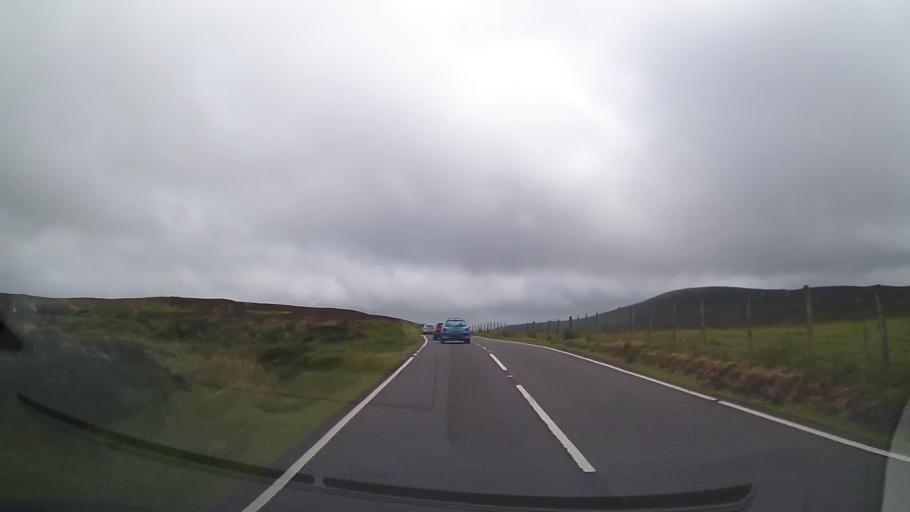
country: GB
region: Wales
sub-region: Denbighshire
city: Llandrillo
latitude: 52.8943
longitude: -3.4869
